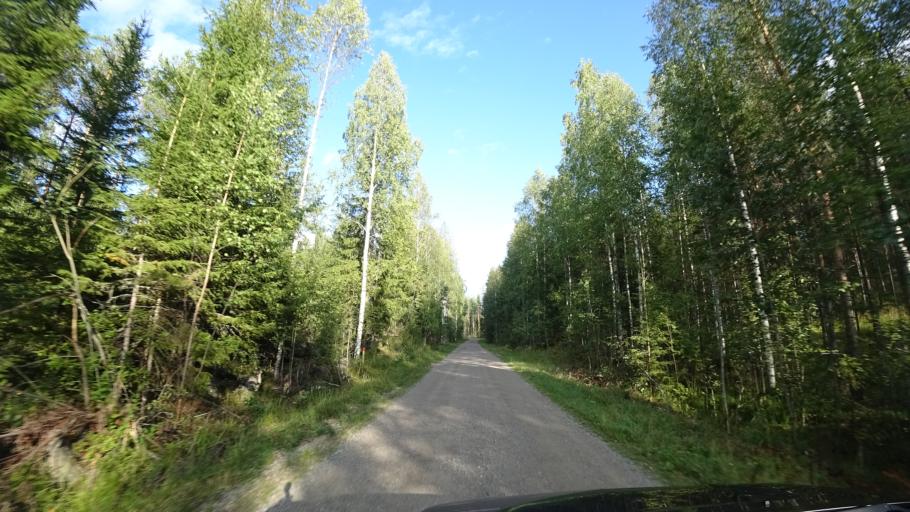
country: FI
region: Paijanne Tavastia
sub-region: Lahti
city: Auttoinen
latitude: 61.2121
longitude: 25.1655
